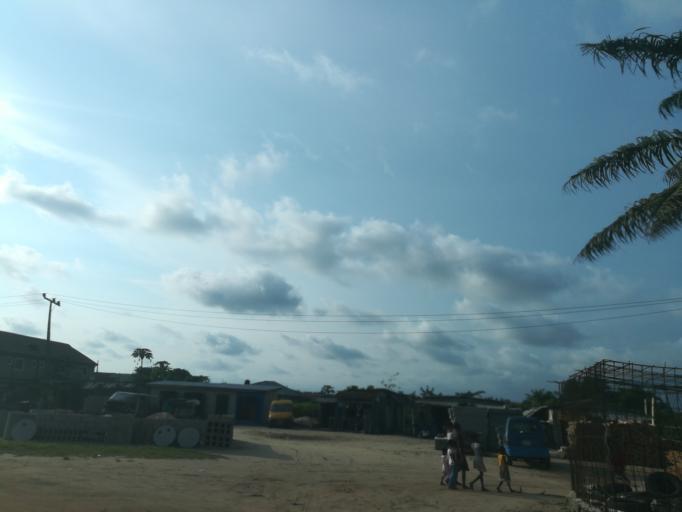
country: NG
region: Ogun
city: Ado Odo
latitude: 6.4768
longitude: 3.0213
